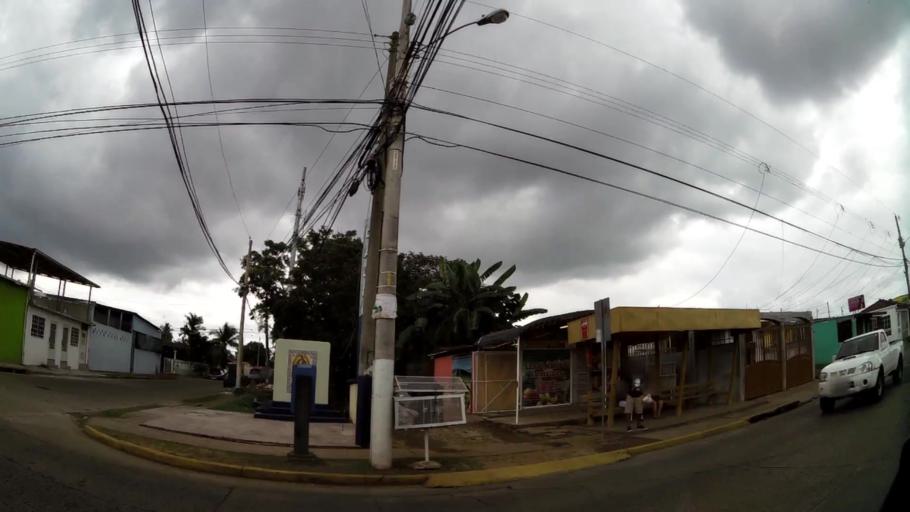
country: PA
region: Panama
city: Tocumen
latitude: 9.0577
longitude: -79.4131
